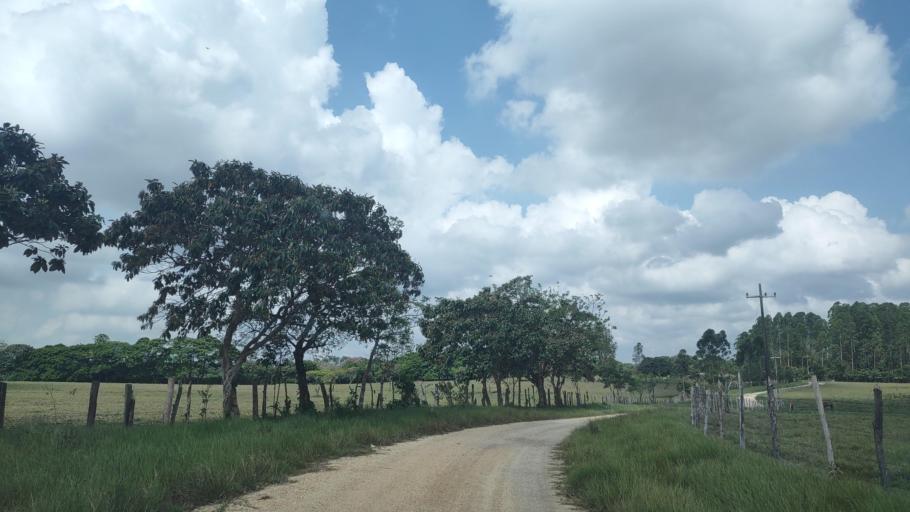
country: MX
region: Veracruz
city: Las Choapas
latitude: 17.9457
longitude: -94.0969
